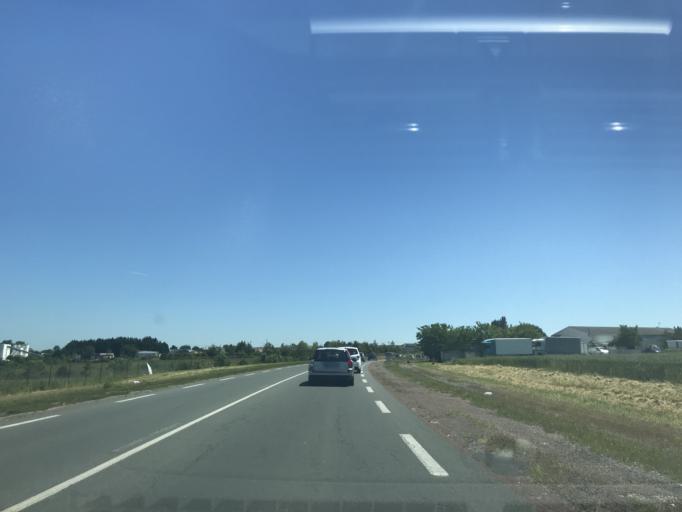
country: FR
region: Poitou-Charentes
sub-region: Departement de la Charente-Maritime
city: Saint-Georges-de-Didonne
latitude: 45.6098
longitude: -0.9775
